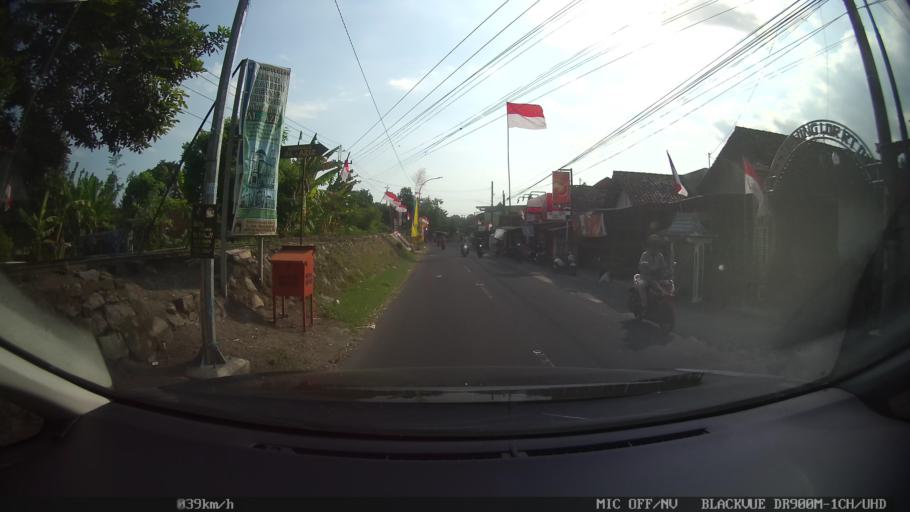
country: ID
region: Daerah Istimewa Yogyakarta
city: Kasihan
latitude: -7.8293
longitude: 110.3403
